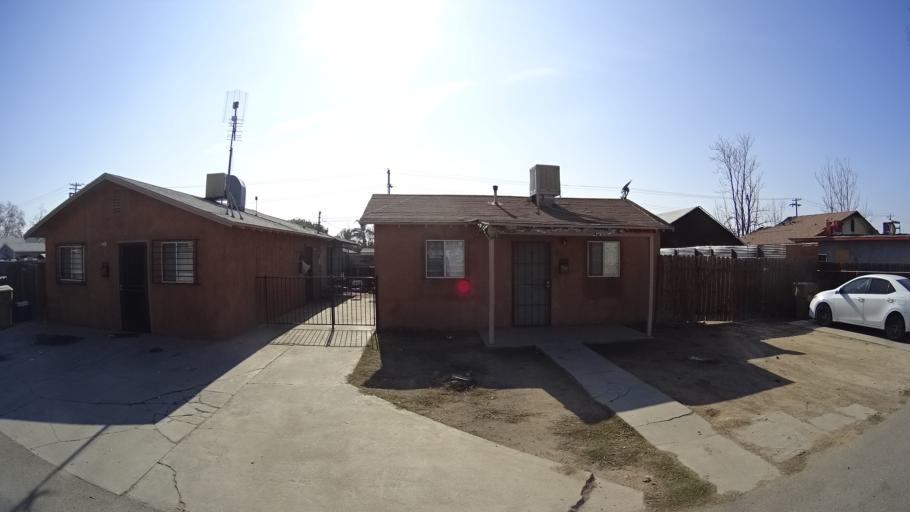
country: US
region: California
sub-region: Kern County
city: Bakersfield
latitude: 35.3808
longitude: -118.9959
